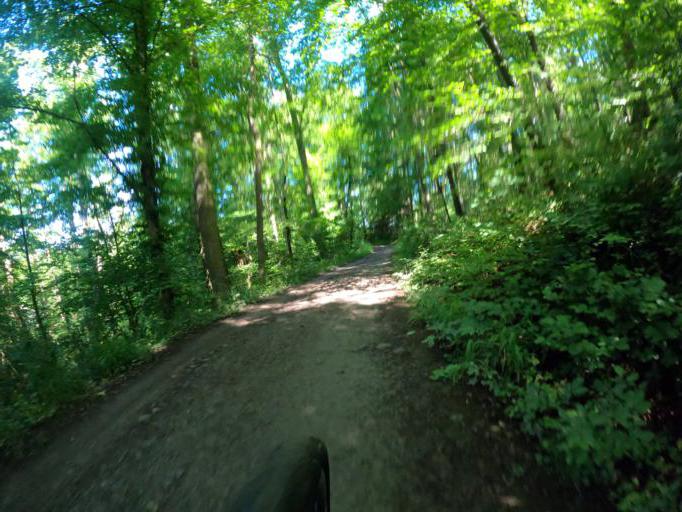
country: DE
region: Baden-Wuerttemberg
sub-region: Regierungsbezirk Stuttgart
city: Gerlingen
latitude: 48.7493
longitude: 9.0909
